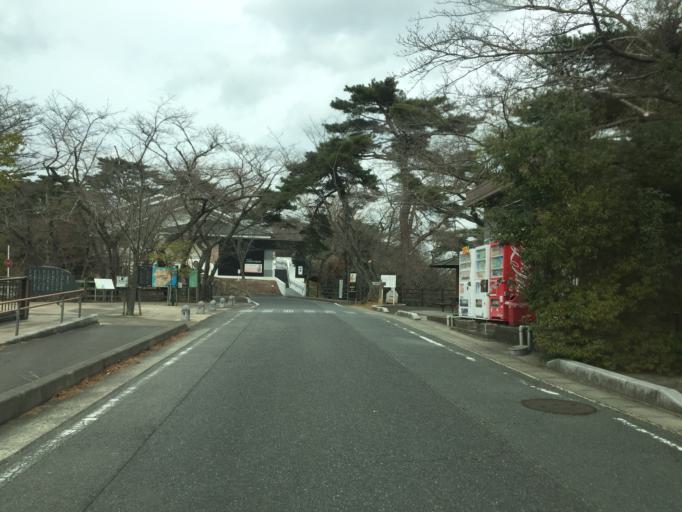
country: JP
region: Ibaraki
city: Kitaibaraki
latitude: 36.8659
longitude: 140.7805
